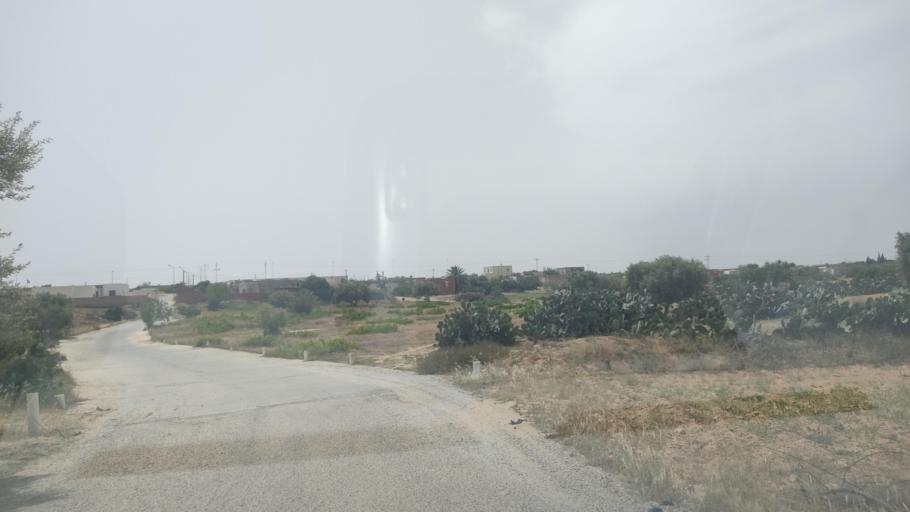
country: TN
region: Safaqis
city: Sfax
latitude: 34.8326
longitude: 10.6001
